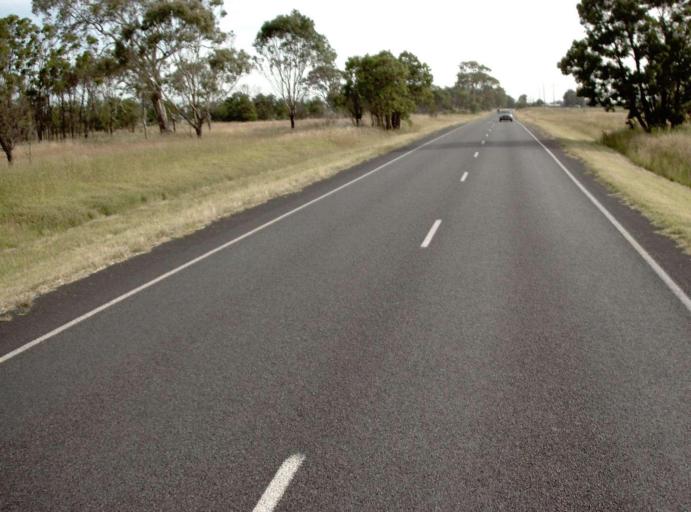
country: AU
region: Victoria
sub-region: Latrobe
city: Traralgon
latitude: -38.0911
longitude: 146.6010
